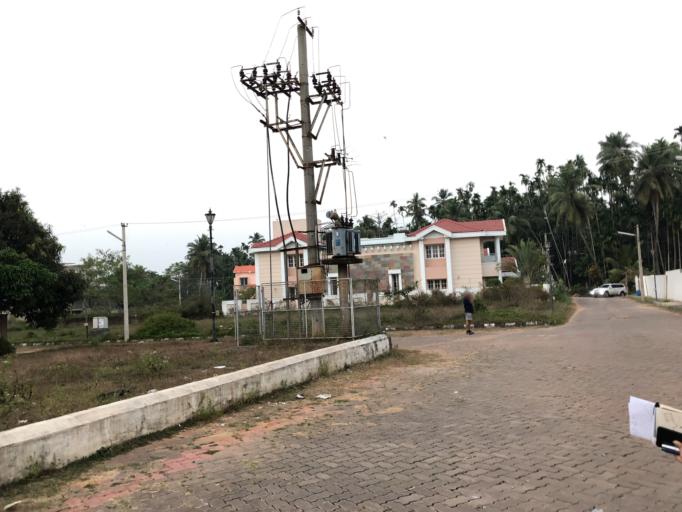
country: IN
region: Karnataka
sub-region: Dakshina Kannada
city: Mangalore
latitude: 12.8906
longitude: 74.8645
